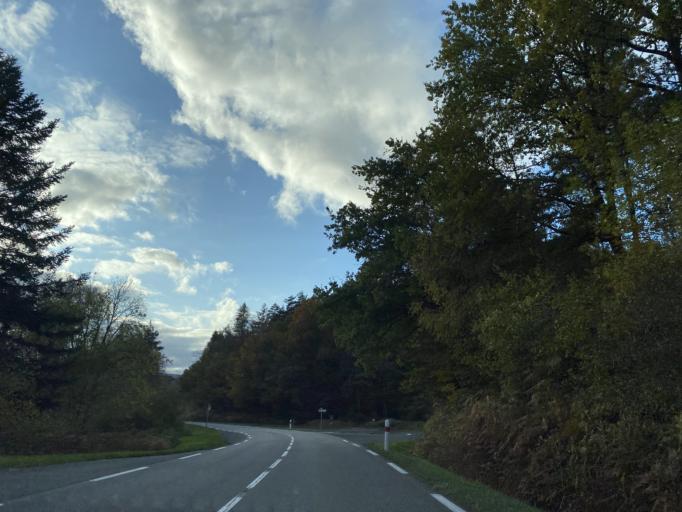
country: FR
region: Auvergne
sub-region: Departement du Puy-de-Dome
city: Job
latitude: 45.6483
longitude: 3.6939
